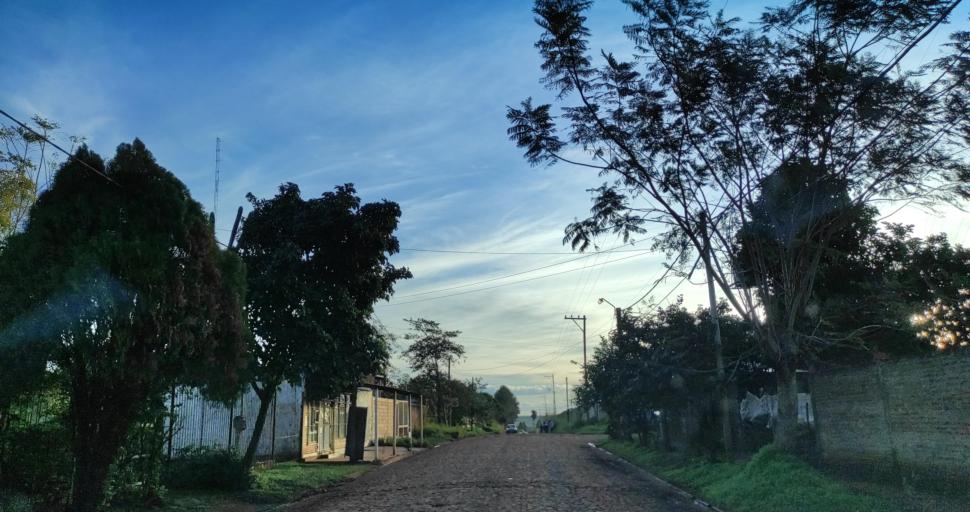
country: AR
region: Misiones
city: Garupa
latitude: -27.4790
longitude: -55.8602
